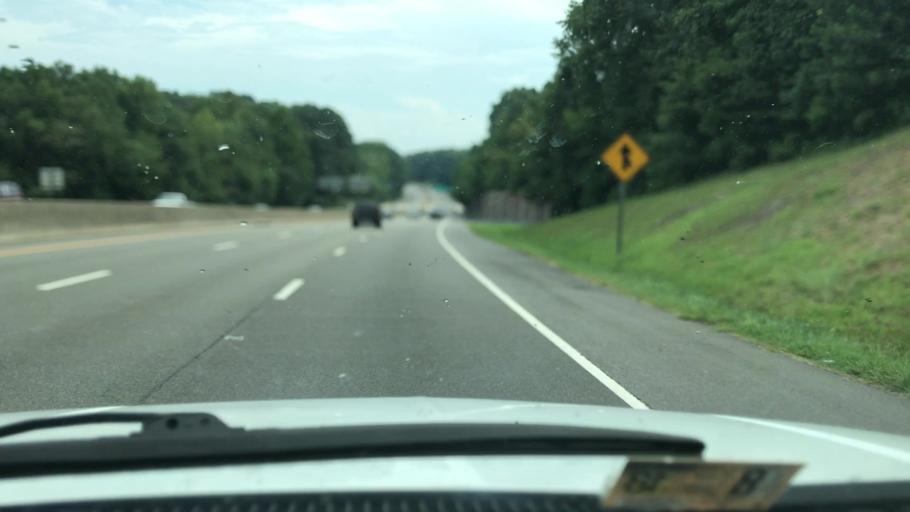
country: US
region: Virginia
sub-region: Chesterfield County
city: Bensley
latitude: 37.4608
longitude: -77.4973
